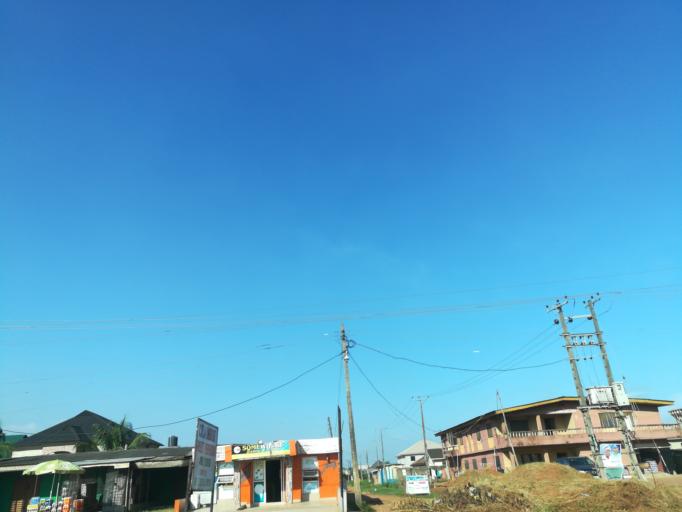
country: NG
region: Lagos
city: Ikorodu
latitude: 6.5765
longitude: 3.5271
